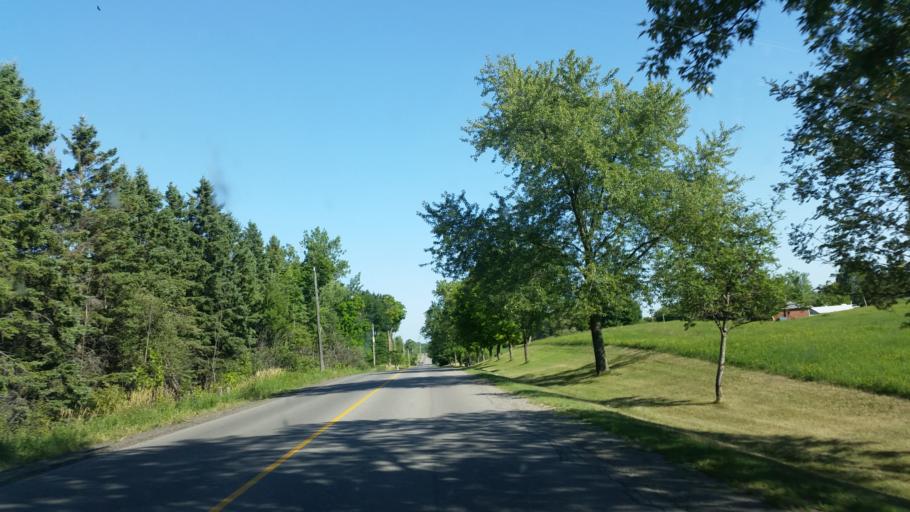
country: CA
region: Ontario
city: Bradford West Gwillimbury
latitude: 43.9520
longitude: -79.7661
